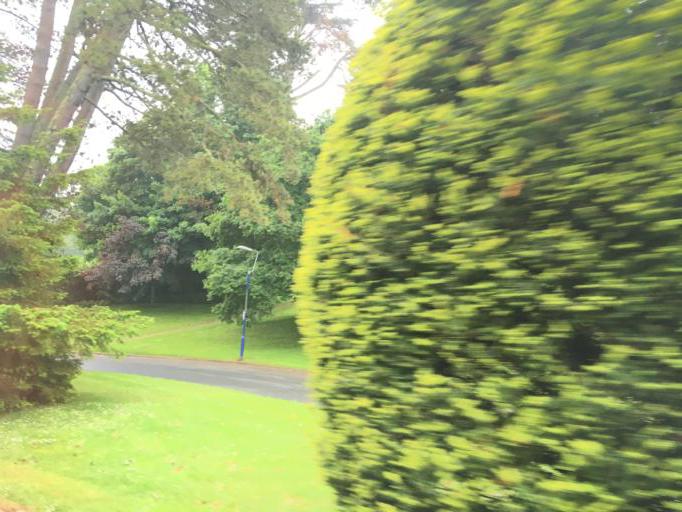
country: GB
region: England
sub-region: Devon
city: Dartmouth
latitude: 50.3556
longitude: -3.5812
